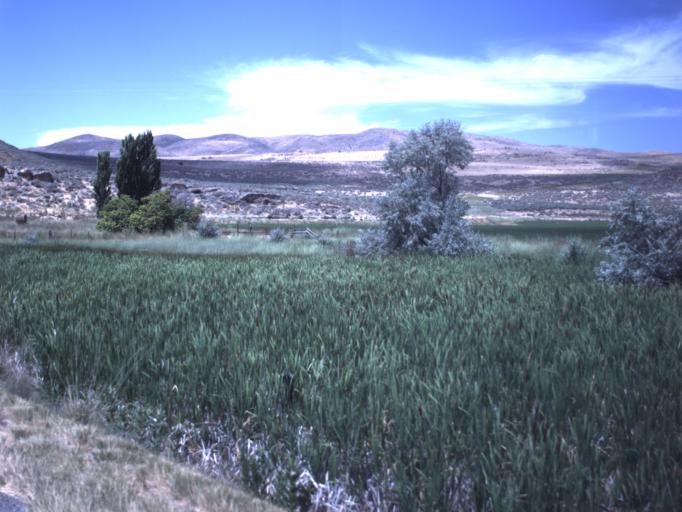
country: US
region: Utah
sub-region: Box Elder County
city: Tremonton
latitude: 41.6369
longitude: -112.3267
